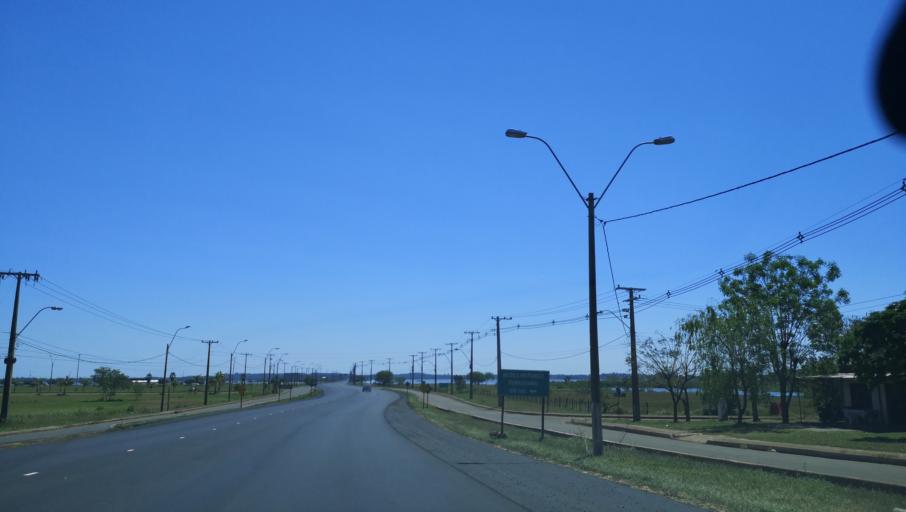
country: PY
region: Itapua
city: Carmen del Parana
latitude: -27.2177
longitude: -56.1460
